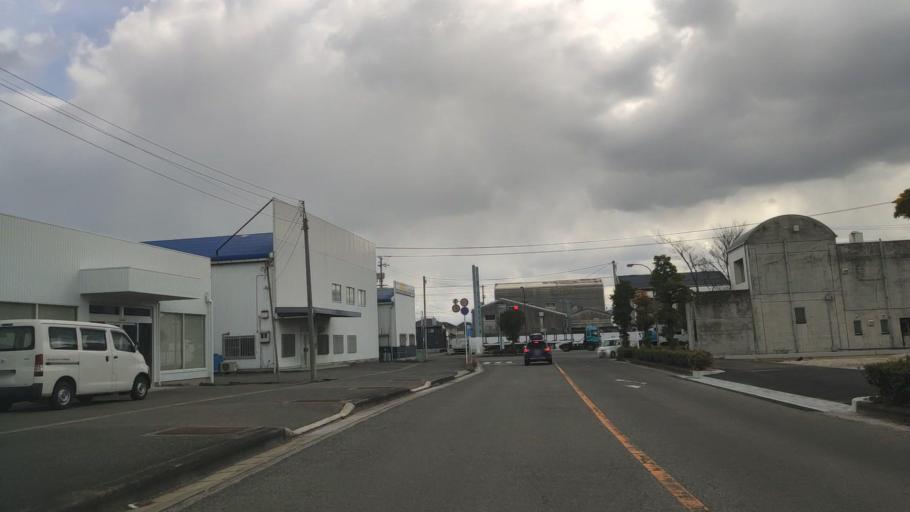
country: JP
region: Ehime
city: Saijo
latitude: 34.0569
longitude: 133.0182
